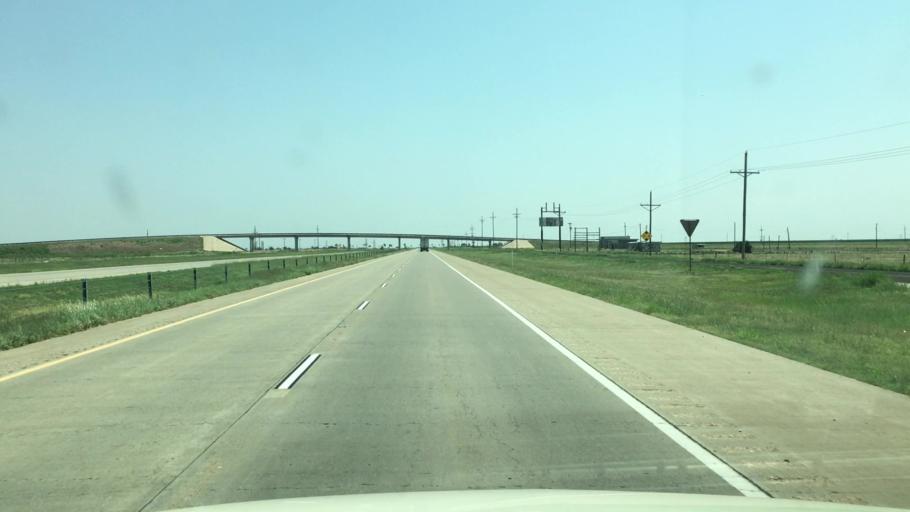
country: US
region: Texas
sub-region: Potter County
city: Bushland
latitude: 35.1970
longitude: -102.1193
